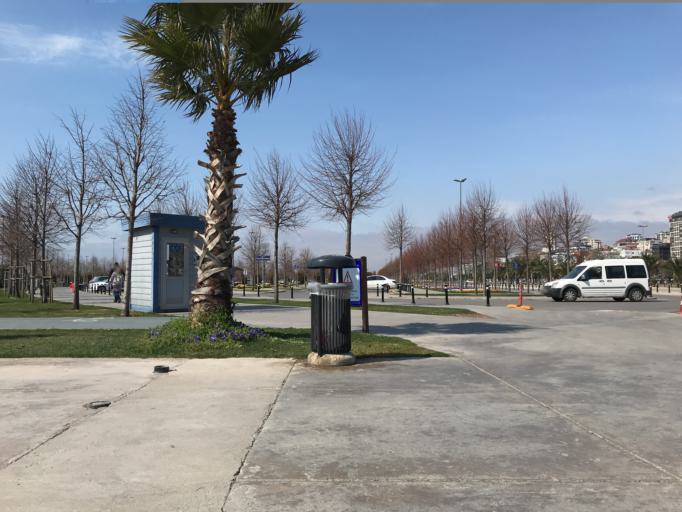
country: TR
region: Istanbul
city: Maltepe
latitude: 40.9247
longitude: 29.1234
